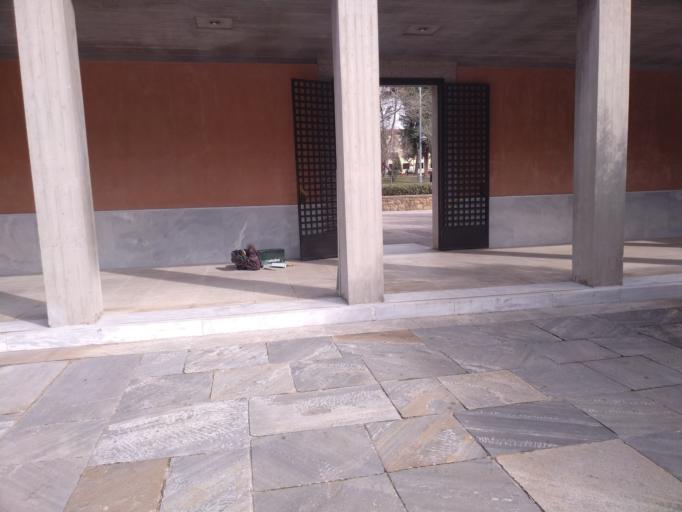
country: GR
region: Central Macedonia
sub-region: Nomos Thessalonikis
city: Agios Pavlos
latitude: 40.6242
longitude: 22.9552
